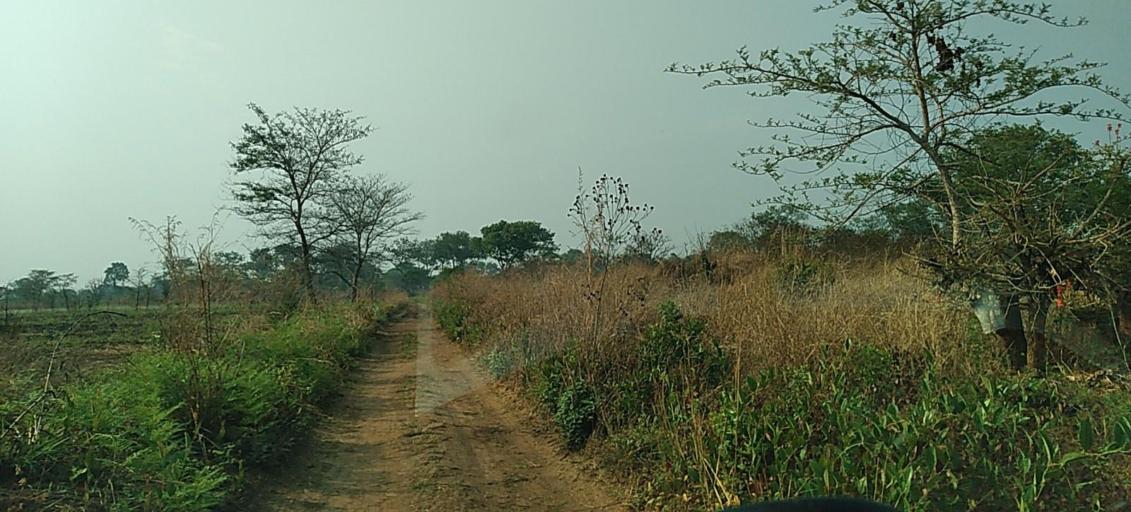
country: ZM
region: North-Western
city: Solwezi
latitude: -12.3805
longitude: 26.5647
